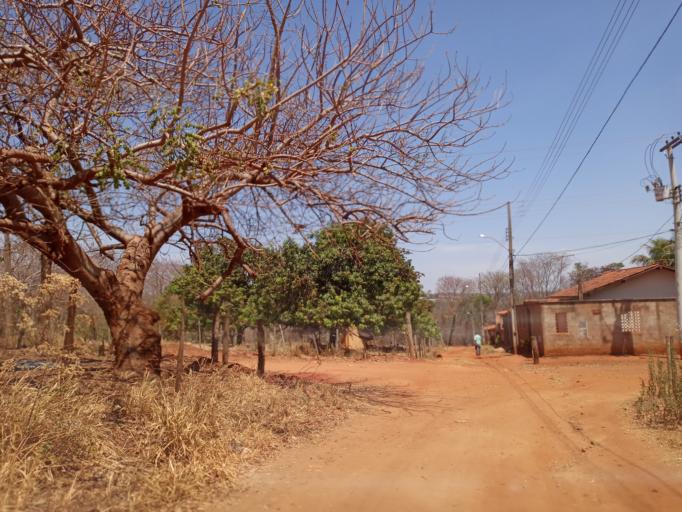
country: BR
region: Minas Gerais
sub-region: Ituiutaba
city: Ituiutaba
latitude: -18.9560
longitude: -49.4665
